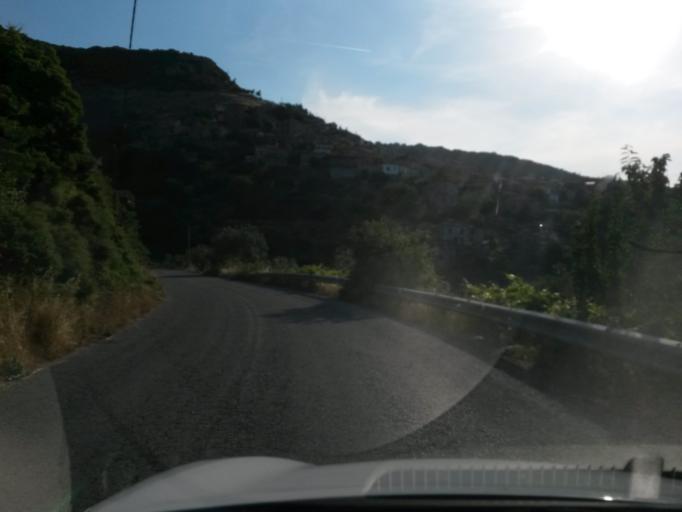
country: GR
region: North Aegean
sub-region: Nomos Lesvou
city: Mantamados
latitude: 39.3613
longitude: 26.2986
